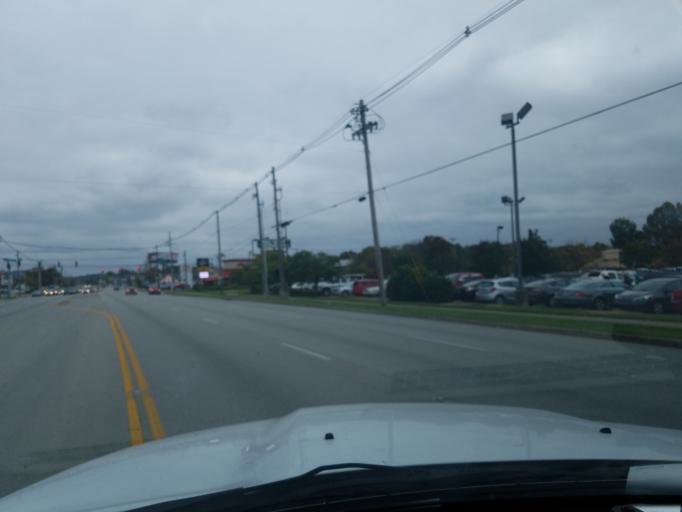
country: US
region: Kentucky
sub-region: Jefferson County
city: Pleasure Ridge Park
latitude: 38.1572
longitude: -85.8341
